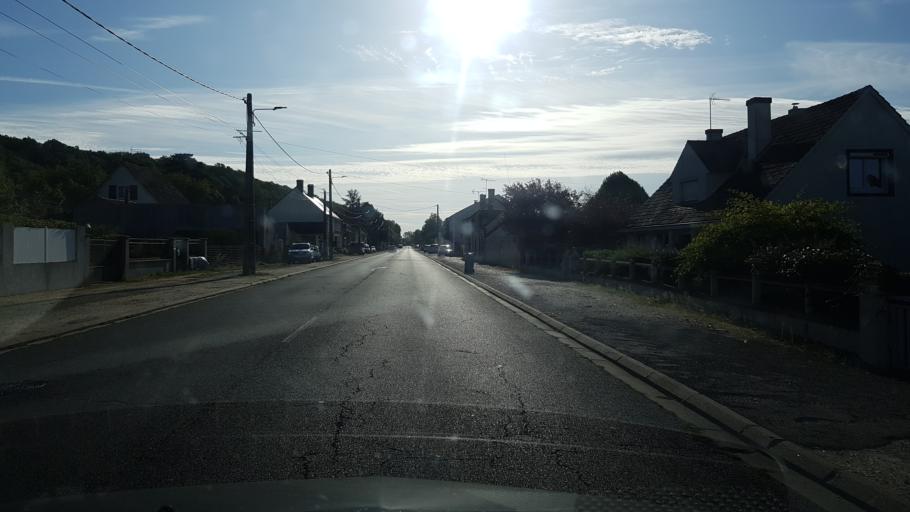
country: FR
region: Centre
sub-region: Departement du Loiret
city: Saint-Martin-sur-Ocre
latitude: 47.6766
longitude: 2.6521
